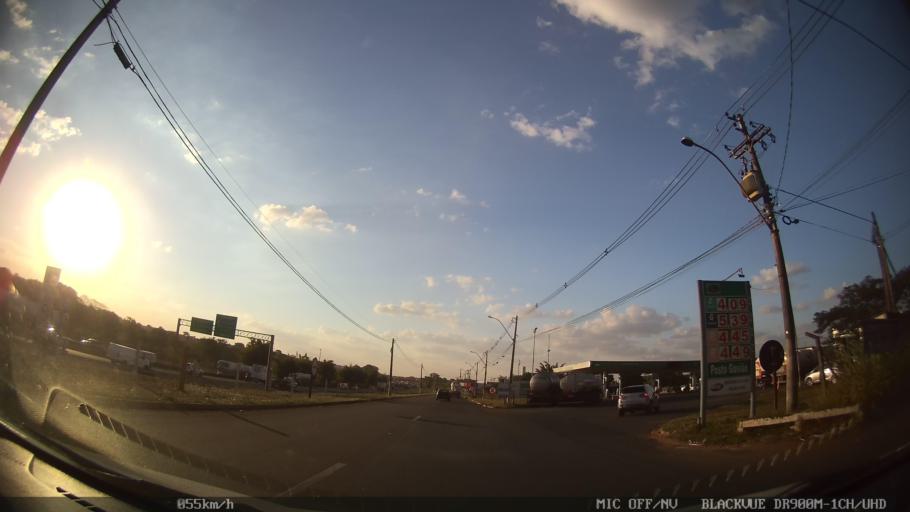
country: BR
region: Sao Paulo
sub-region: Ribeirao Preto
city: Ribeirao Preto
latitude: -21.1609
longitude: -47.7558
